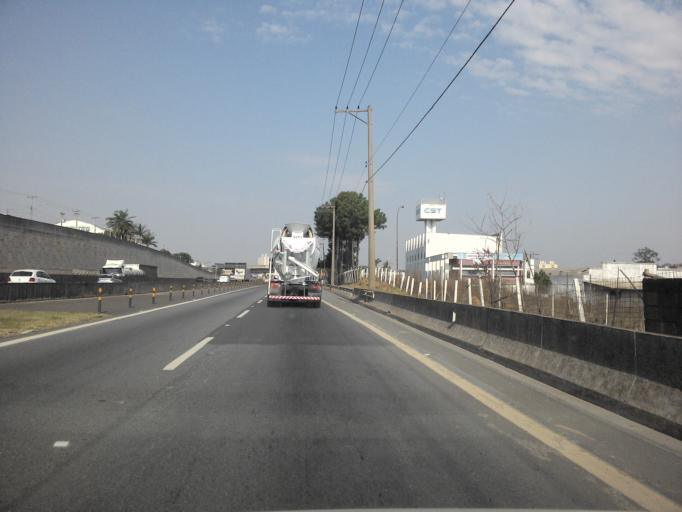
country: BR
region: Sao Paulo
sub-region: Campinas
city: Campinas
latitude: -22.9069
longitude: -47.1057
